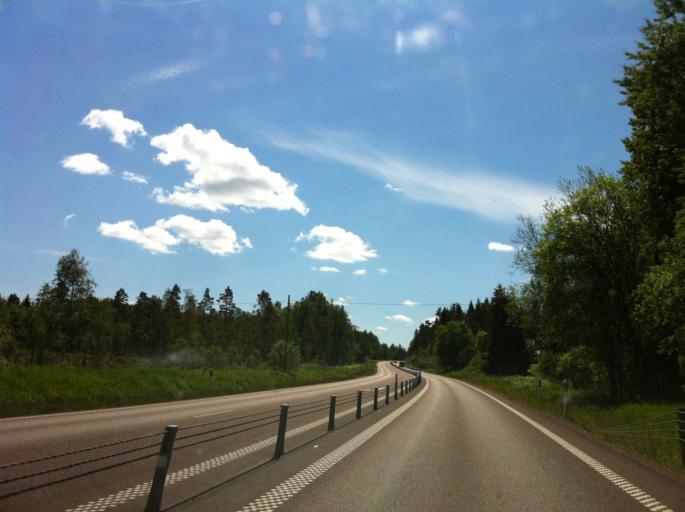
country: SE
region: Vaestra Goetaland
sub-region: Melleruds Kommun
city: Mellerud
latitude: 58.8155
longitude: 12.5232
